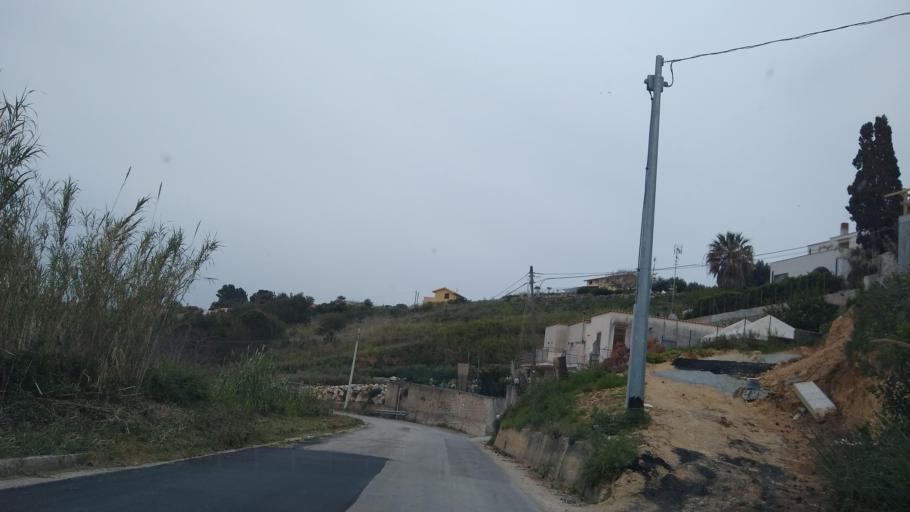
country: IT
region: Sicily
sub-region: Trapani
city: Castellammare del Golfo
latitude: 38.0216
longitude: 12.8974
